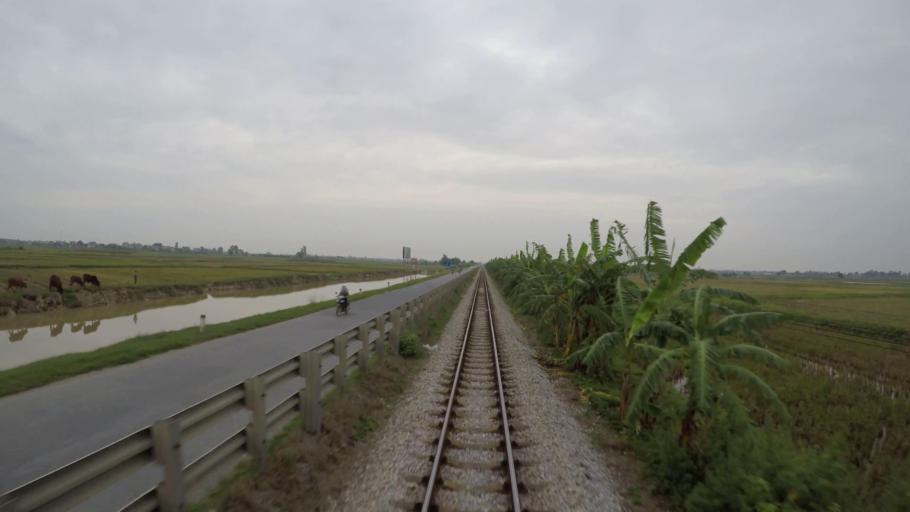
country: VN
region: Hung Yen
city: Ban Yen Nhan
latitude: 20.9819
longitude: 106.0772
